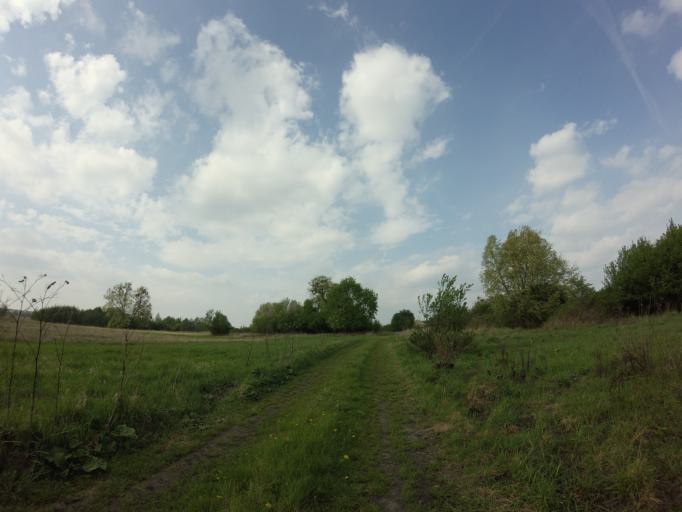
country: PL
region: West Pomeranian Voivodeship
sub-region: Powiat choszczenski
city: Choszczno
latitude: 53.1711
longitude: 15.3913
